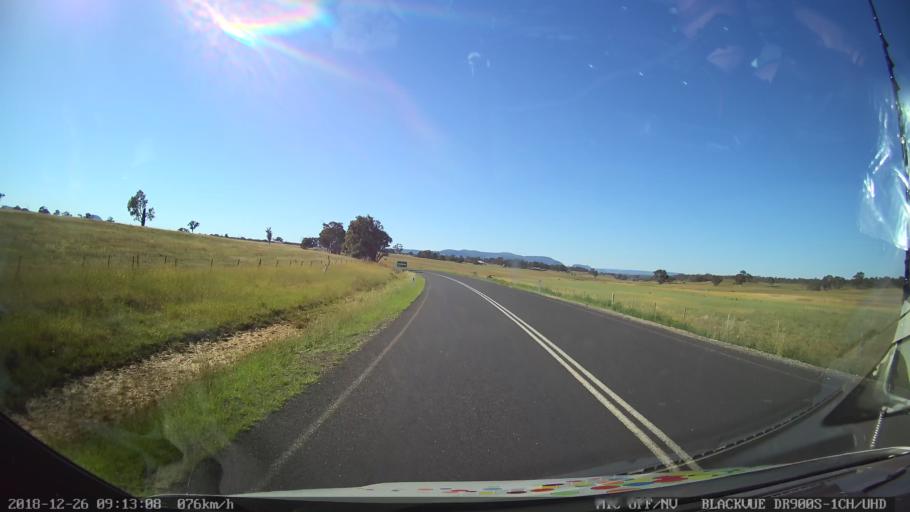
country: AU
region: New South Wales
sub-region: Mid-Western Regional
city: Kandos
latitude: -32.7647
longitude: 149.9777
